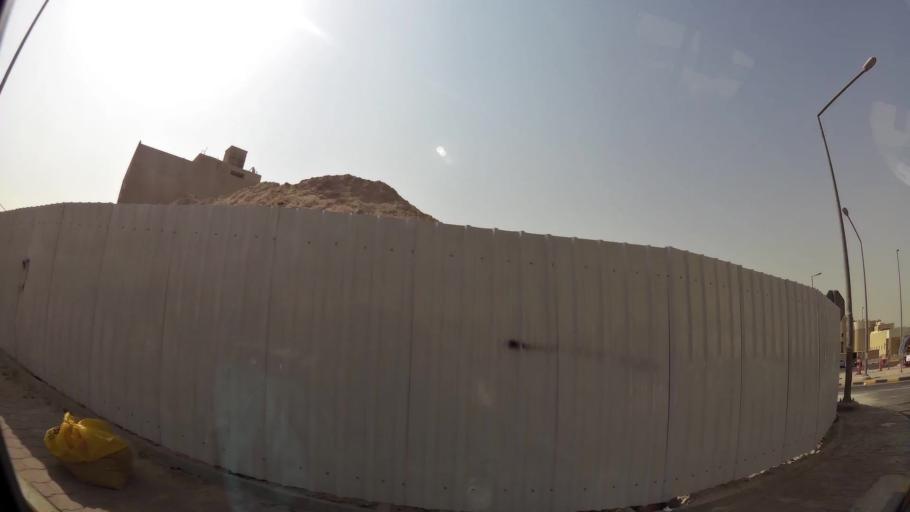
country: KW
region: Muhafazat al Jahra'
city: Al Jahra'
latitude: 29.3391
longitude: 47.7742
